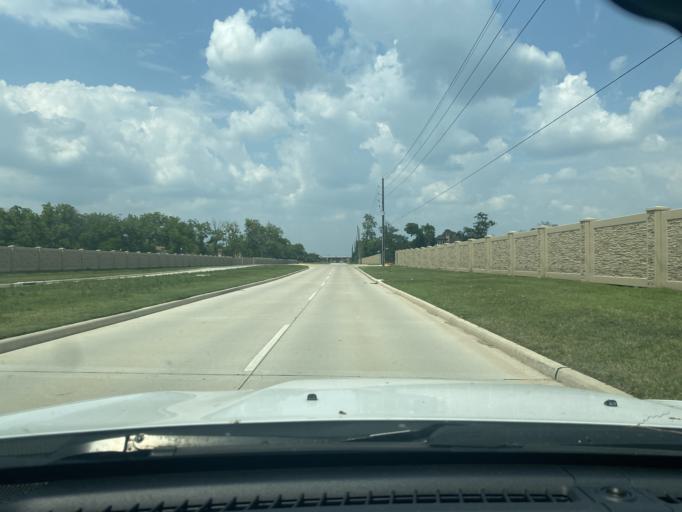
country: US
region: Texas
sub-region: Fort Bend County
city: Greatwood
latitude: 29.5494
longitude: -95.7202
